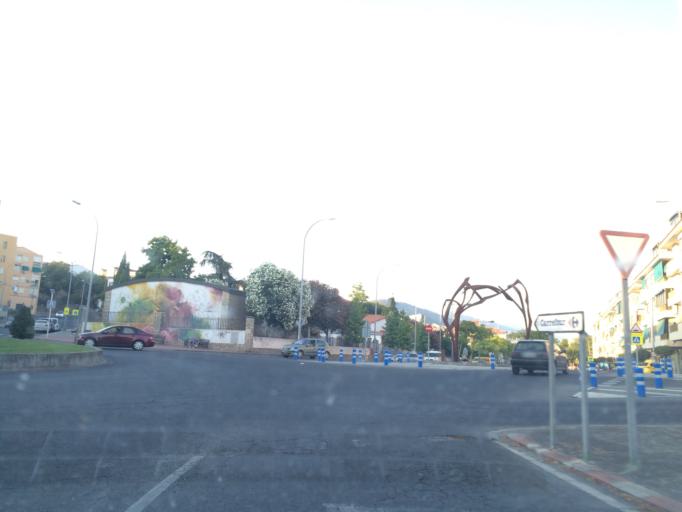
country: ES
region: Extremadura
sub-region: Provincia de Caceres
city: Plasencia
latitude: 40.0384
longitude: -6.0825
